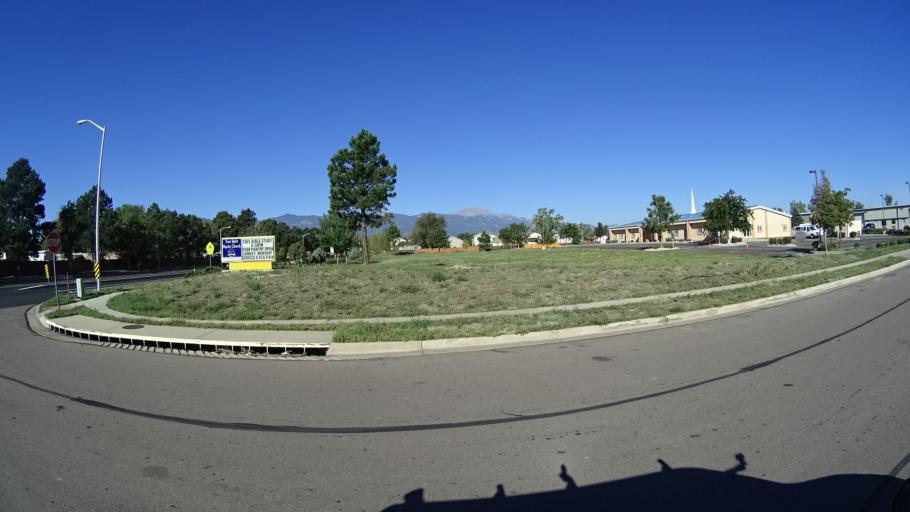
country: US
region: Colorado
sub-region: El Paso County
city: Stratmoor
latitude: 38.7991
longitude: -104.7329
